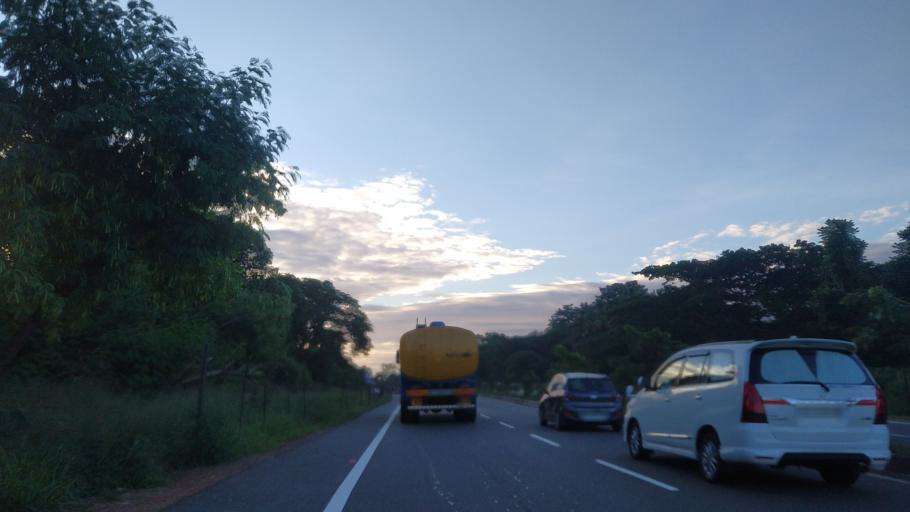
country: IN
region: Kerala
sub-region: Ernakulam
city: Elur
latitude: 10.0687
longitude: 76.3084
